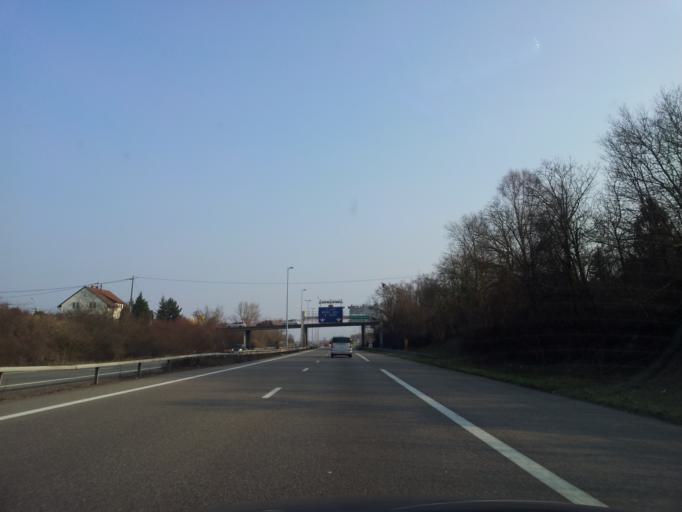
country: FR
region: Alsace
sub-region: Departement du Haut-Rhin
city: Blotzheim
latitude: 47.6083
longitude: 7.5256
